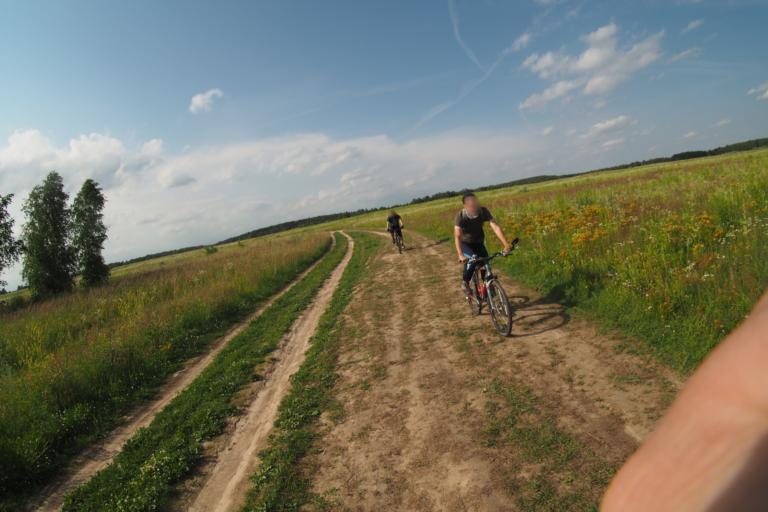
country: RU
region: Moskovskaya
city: Pavlovskaya Sloboda
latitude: 55.8350
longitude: 37.0794
